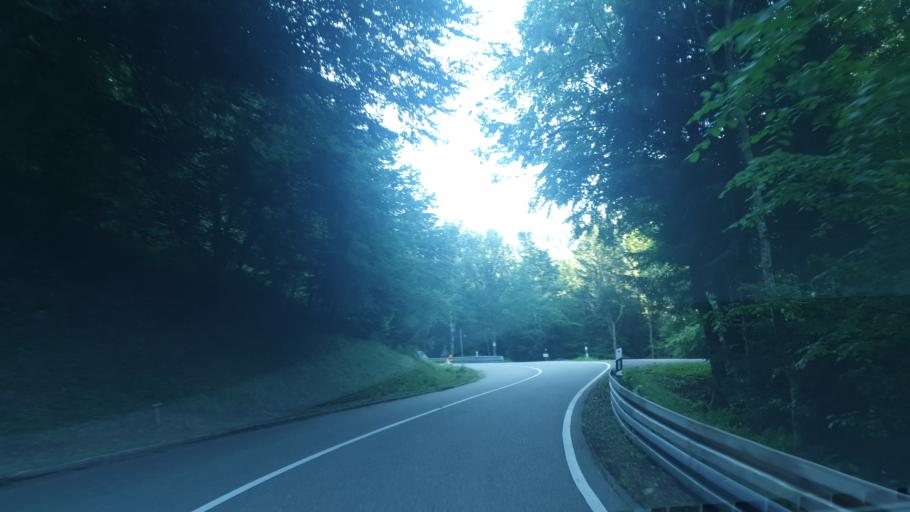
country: DE
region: Baden-Wuerttemberg
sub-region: Freiburg Region
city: Horben
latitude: 47.9213
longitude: 7.8795
